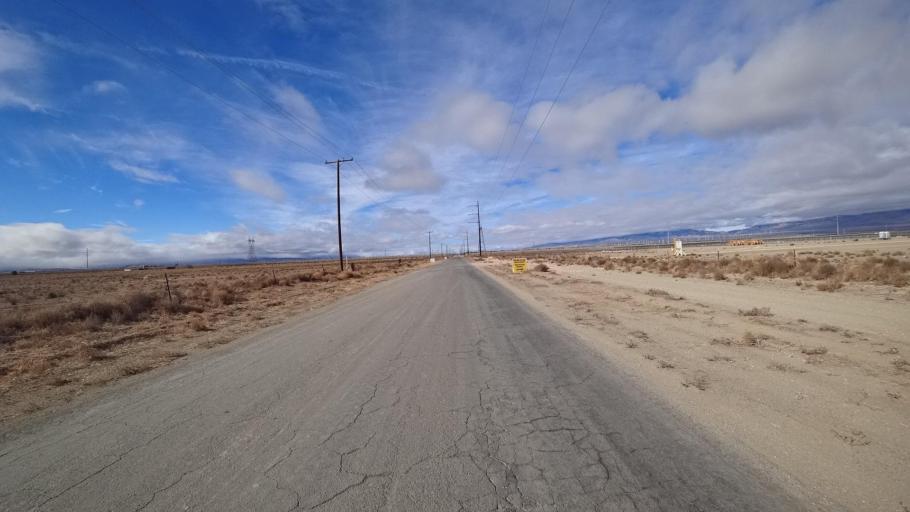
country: US
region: California
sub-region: Kern County
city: Rosamond
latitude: 34.8345
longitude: -118.3124
